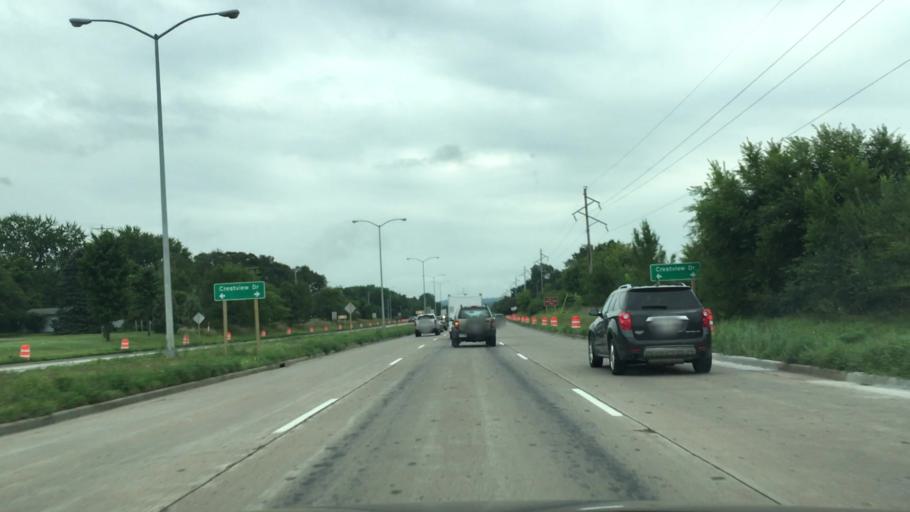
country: US
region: Wisconsin
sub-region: Eau Claire County
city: Eau Claire
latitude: 44.8130
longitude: -91.5389
